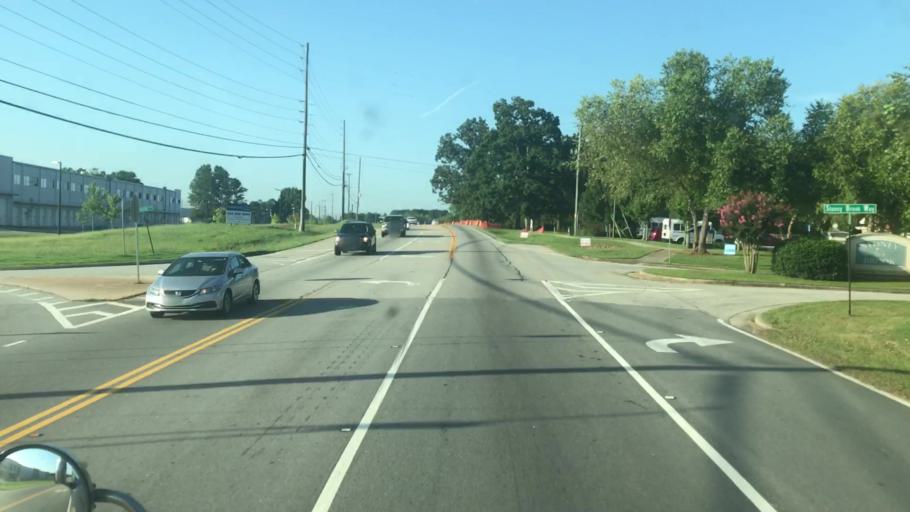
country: US
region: Georgia
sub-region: Henry County
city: McDonough
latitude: 33.3981
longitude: -84.1741
